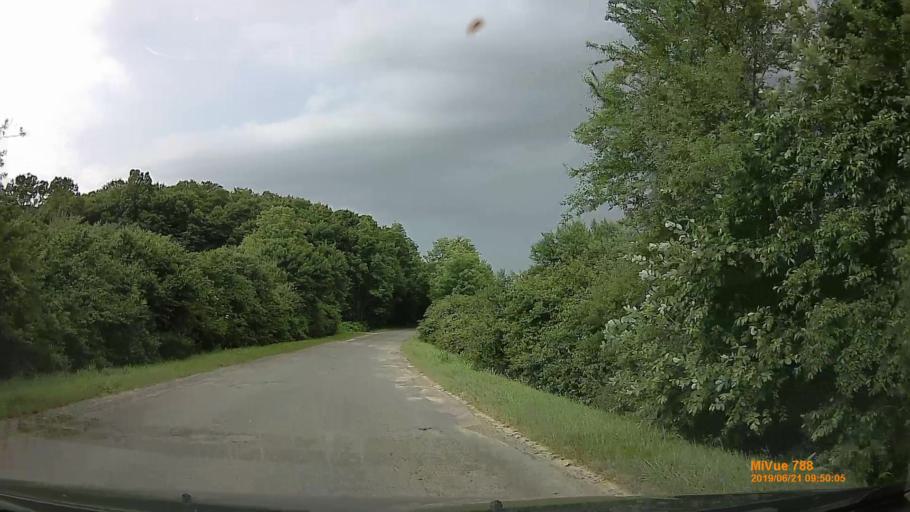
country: HU
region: Baranya
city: Sasd
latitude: 46.2627
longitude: 18.0345
